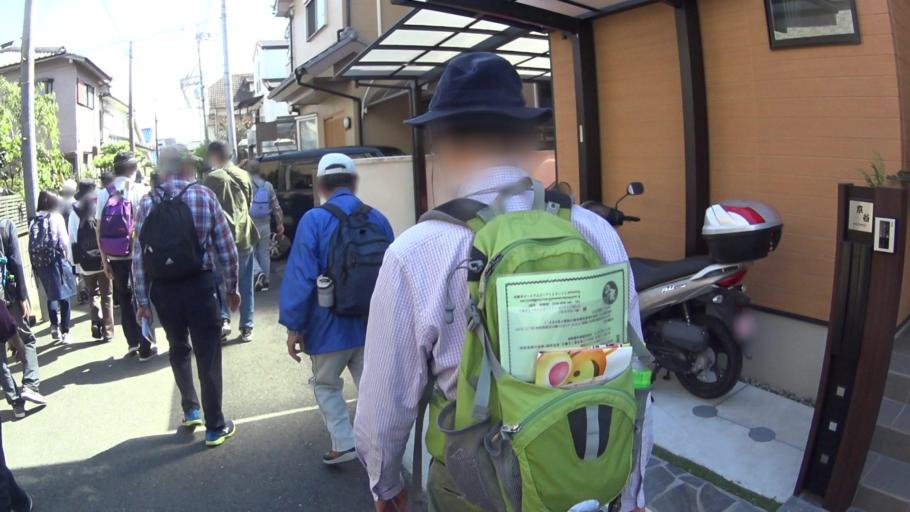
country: JP
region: Osaka
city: Kashihara
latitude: 34.5564
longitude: 135.6053
